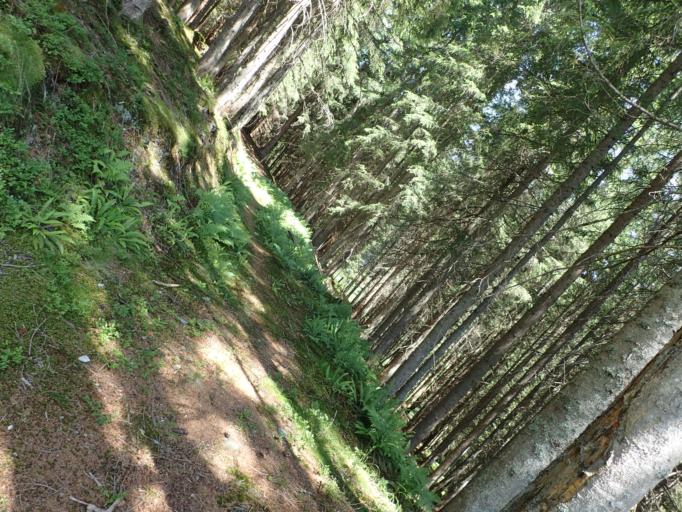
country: AT
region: Salzburg
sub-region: Politischer Bezirk Sankt Johann im Pongau
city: Filzmoos
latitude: 47.4527
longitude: 13.4684
